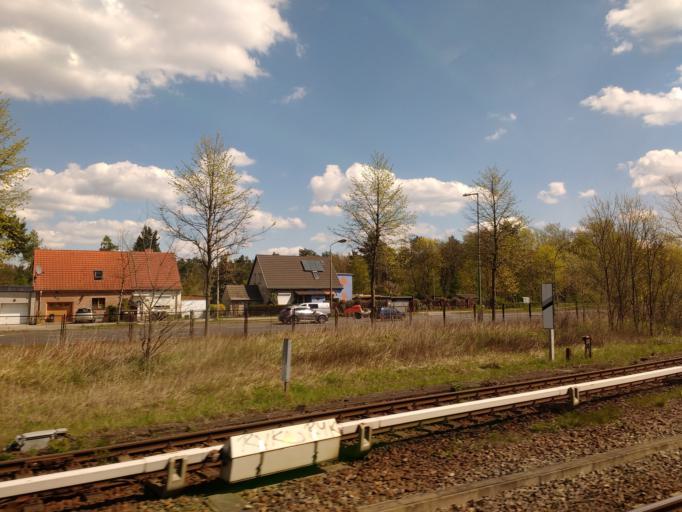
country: DE
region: Berlin
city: Adlershof
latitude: 52.4214
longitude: 13.5615
